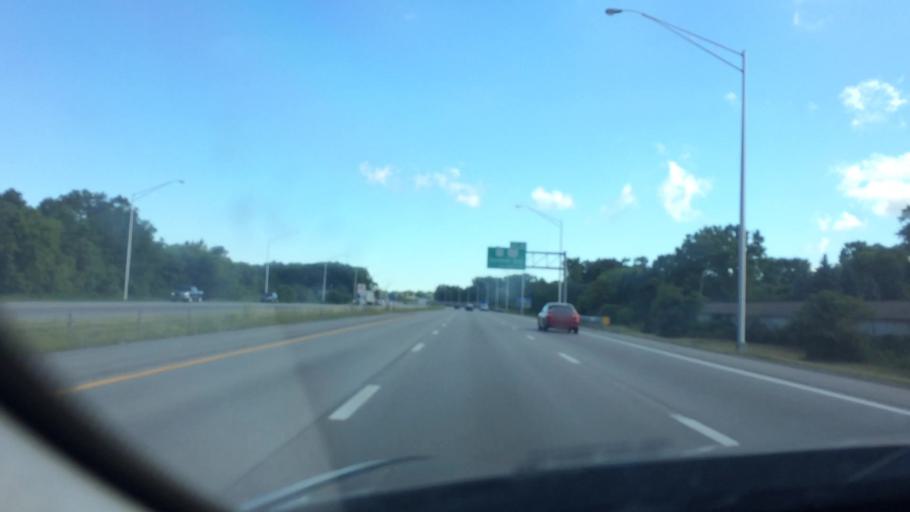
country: US
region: Ohio
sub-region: Lucas County
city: Holland
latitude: 41.6630
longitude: -83.6940
